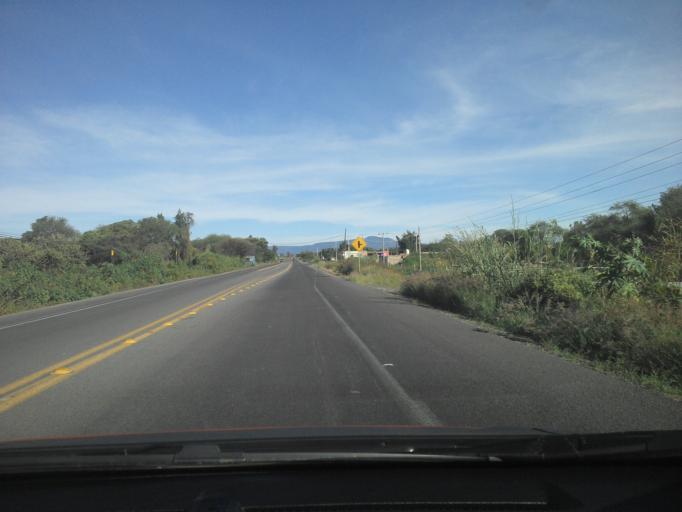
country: MX
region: Jalisco
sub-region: Teuchitlan
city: La Estanzuela
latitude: 20.6738
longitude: -103.8277
